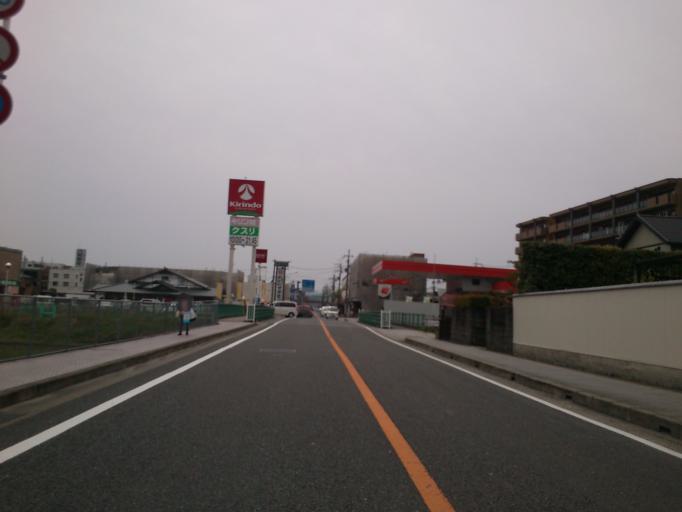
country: JP
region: Kyoto
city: Yawata
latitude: 34.8811
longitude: 135.7067
